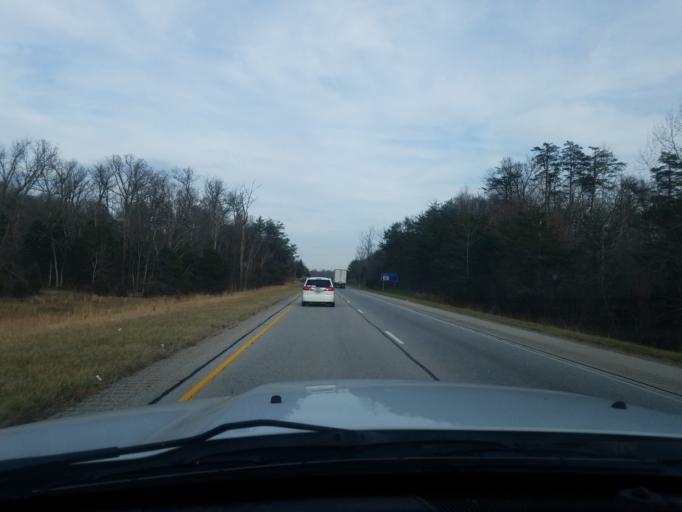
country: US
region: Indiana
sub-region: Floyd County
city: Georgetown
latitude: 38.2795
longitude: -85.9490
